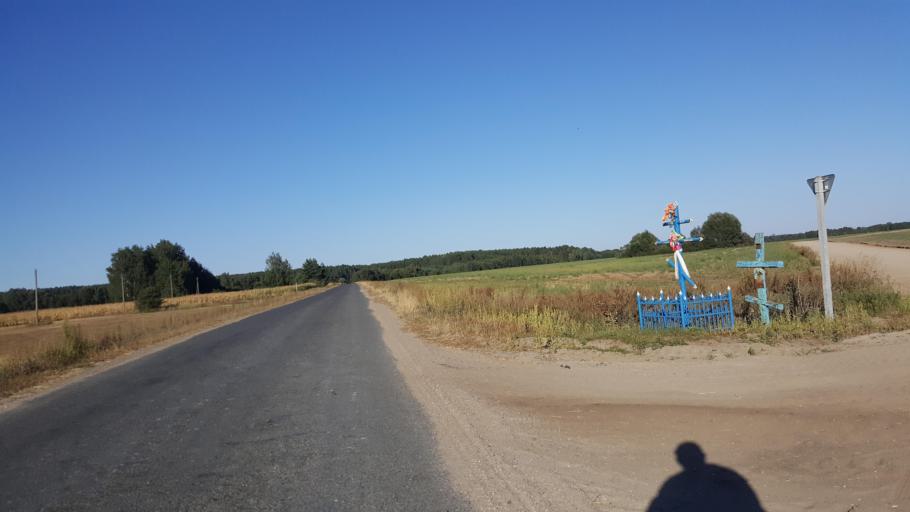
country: BY
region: Brest
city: Vysokaye
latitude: 52.3300
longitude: 23.2726
